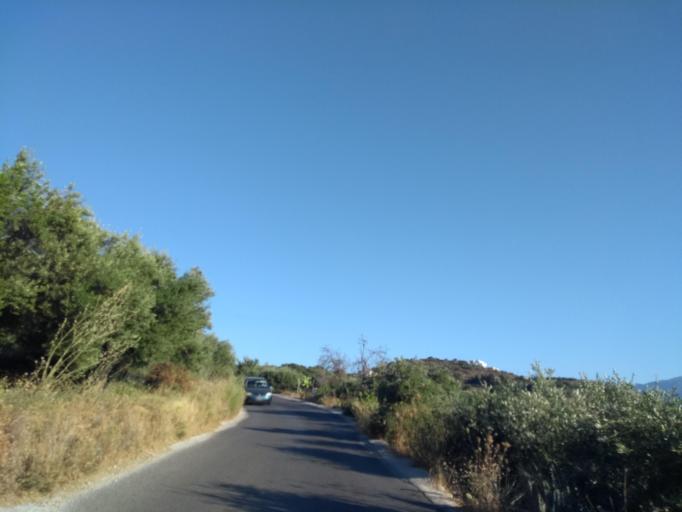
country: GR
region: Crete
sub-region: Nomos Chanias
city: Kalivai
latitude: 35.4373
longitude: 24.1732
